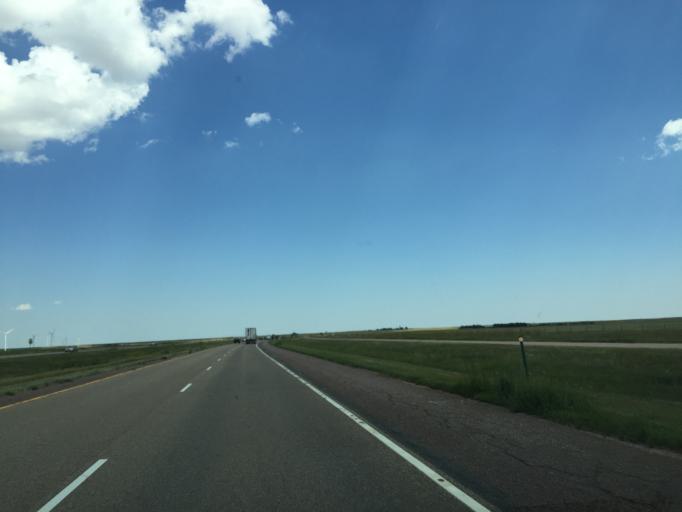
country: US
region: Colorado
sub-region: Lincoln County
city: Hugo
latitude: 39.2788
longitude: -103.4114
